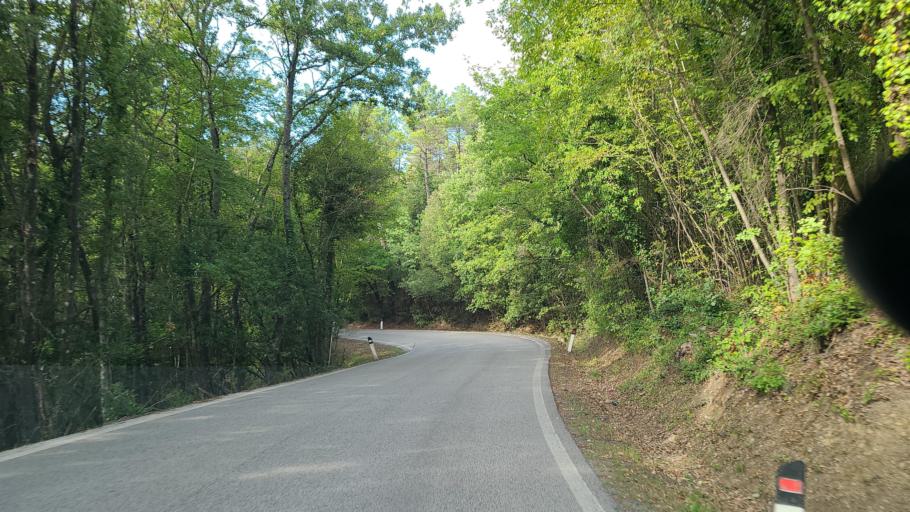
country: IT
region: Tuscany
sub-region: Provincia di Siena
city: San Gimignano
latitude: 43.4168
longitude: 10.9763
